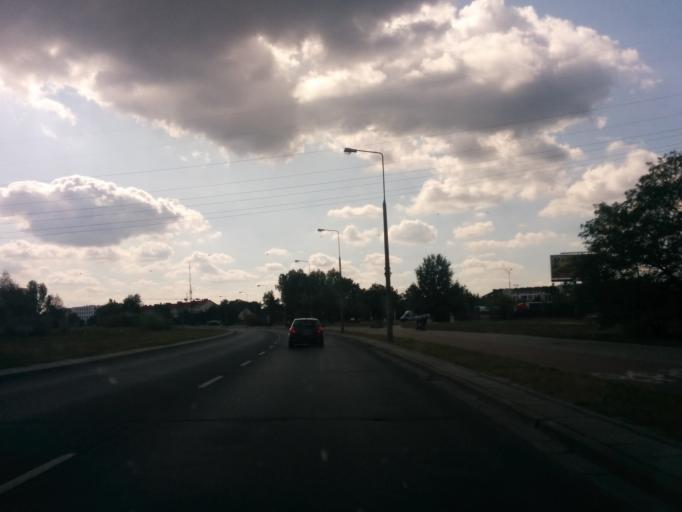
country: PL
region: Masovian Voivodeship
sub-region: Warszawa
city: Bialoleka
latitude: 52.3266
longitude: 20.9405
